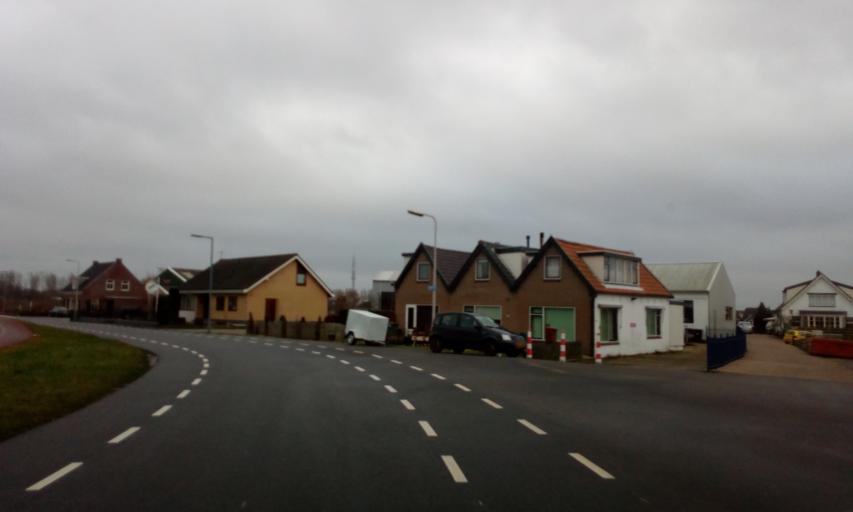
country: NL
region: South Holland
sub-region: Gemeente Capelle aan den IJssel
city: Capelle aan den IJssel
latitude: 51.9759
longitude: 4.5935
